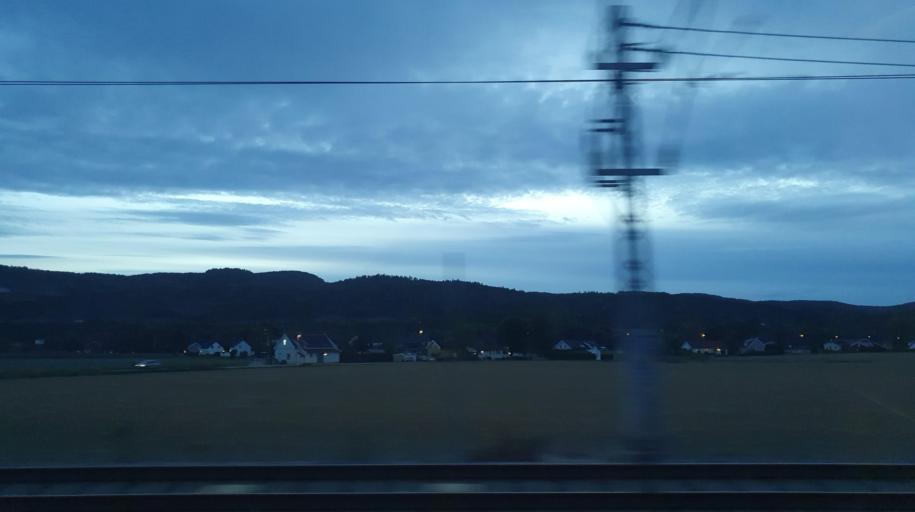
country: NO
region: Vestfold
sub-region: Sande
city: Sande
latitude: 59.5884
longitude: 10.2028
